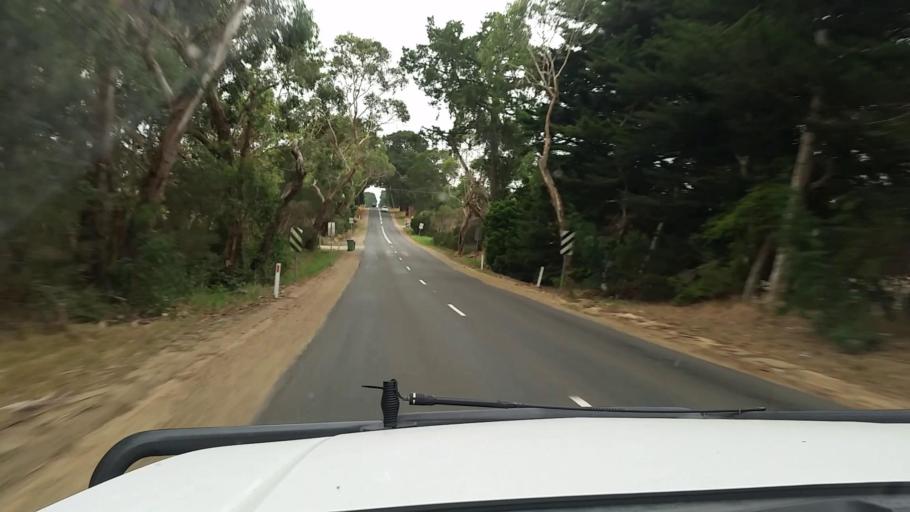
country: AU
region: Victoria
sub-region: Mornington Peninsula
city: Hastings
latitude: -38.3145
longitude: 145.1457
